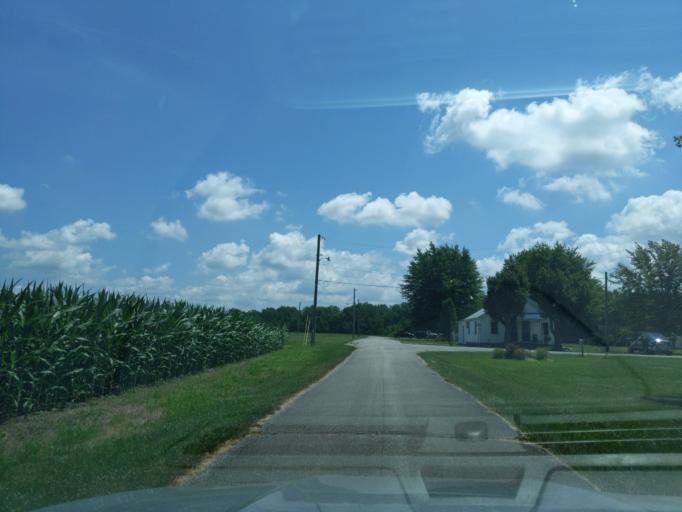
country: US
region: Indiana
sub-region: Decatur County
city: Greensburg
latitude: 39.2123
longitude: -85.4318
